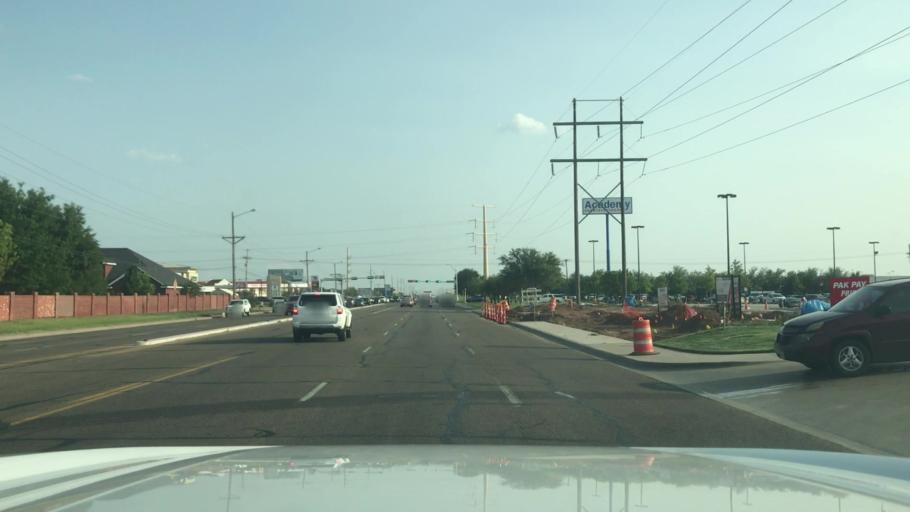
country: US
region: Texas
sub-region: Potter County
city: Amarillo
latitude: 35.1637
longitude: -101.9382
